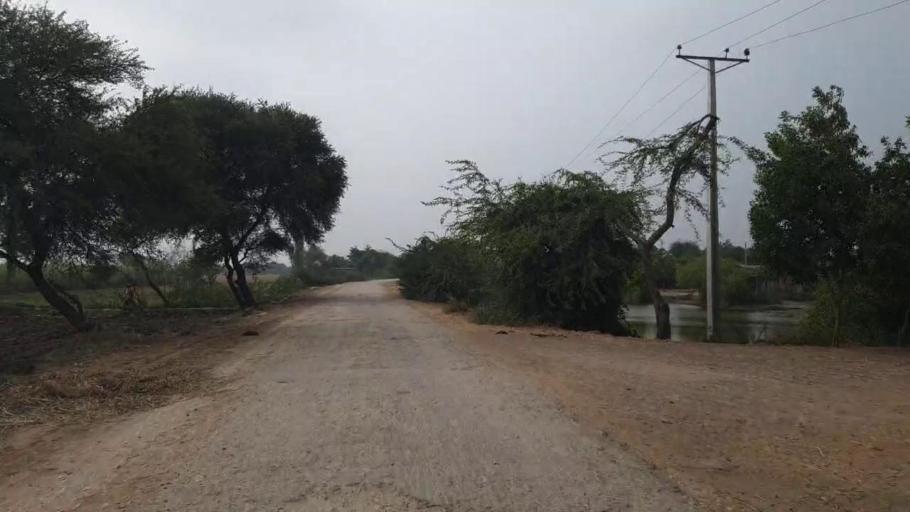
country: PK
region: Sindh
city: Matli
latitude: 24.9527
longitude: 68.5816
